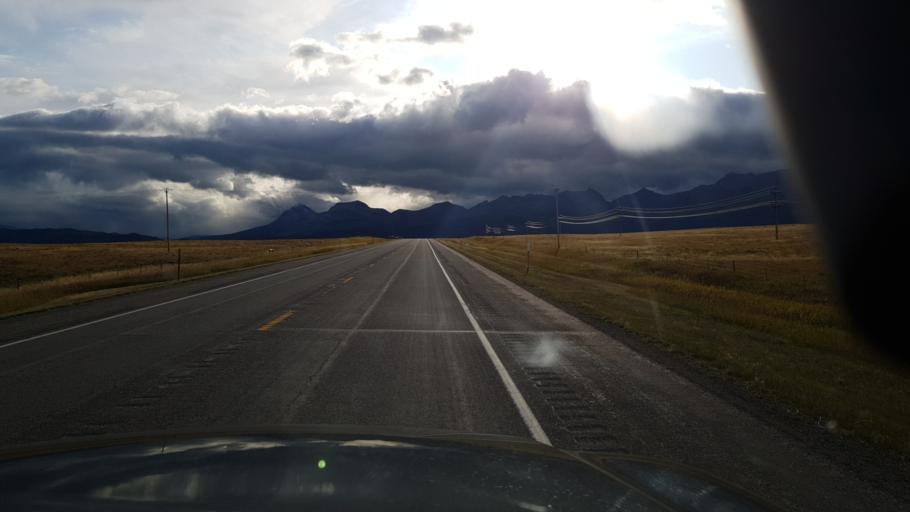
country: US
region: Montana
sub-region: Glacier County
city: South Browning
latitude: 48.4642
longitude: -113.1620
